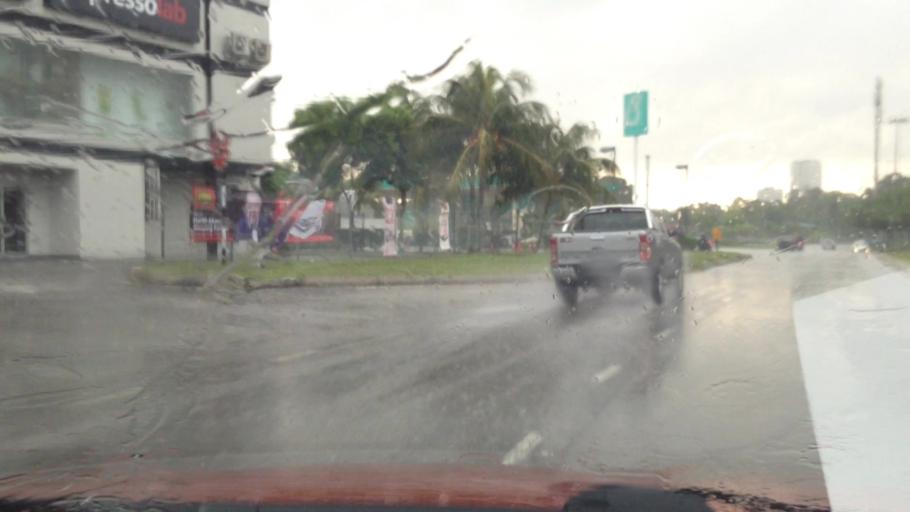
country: MY
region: Selangor
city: Subang Jaya
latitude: 3.0223
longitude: 101.5876
